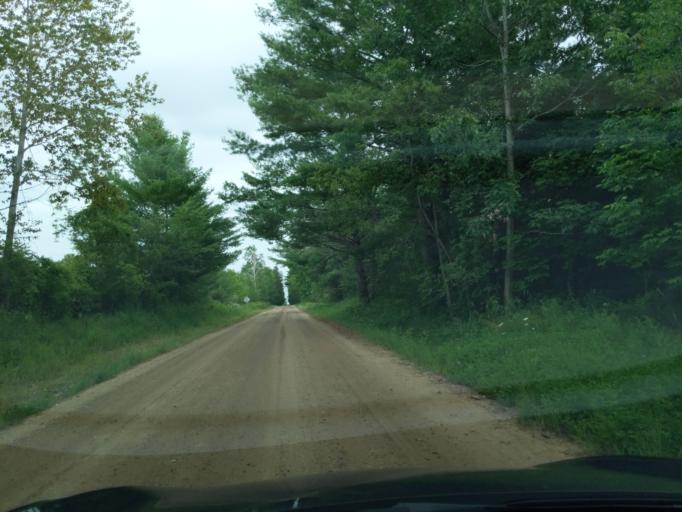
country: US
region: Michigan
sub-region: Clare County
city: Harrison
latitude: 43.9878
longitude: -85.0072
